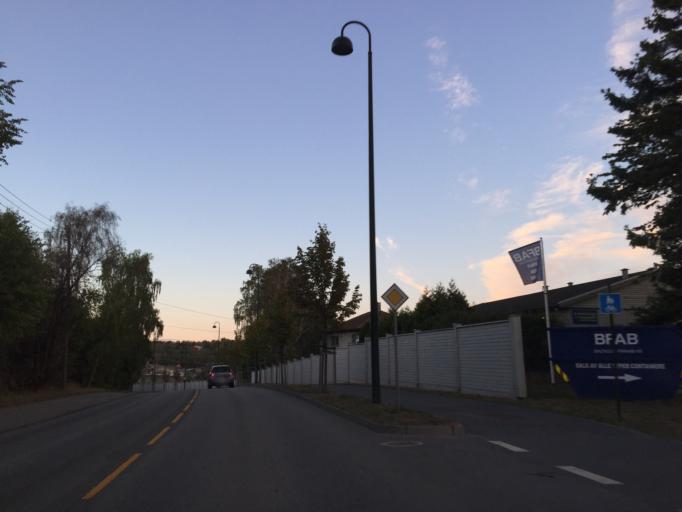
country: NO
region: Ostfold
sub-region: Moss
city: Moss
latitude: 59.4470
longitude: 10.6865
